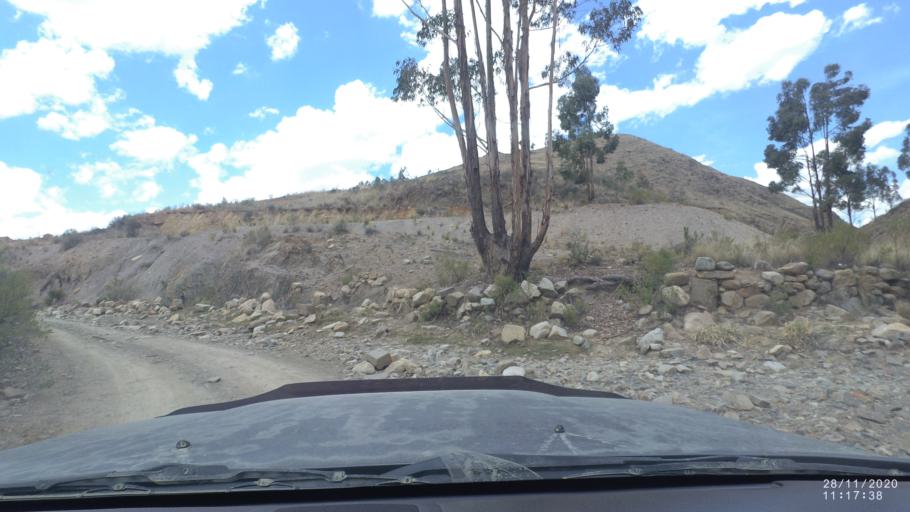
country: BO
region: Cochabamba
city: Tarata
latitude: -17.7532
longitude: -66.0772
